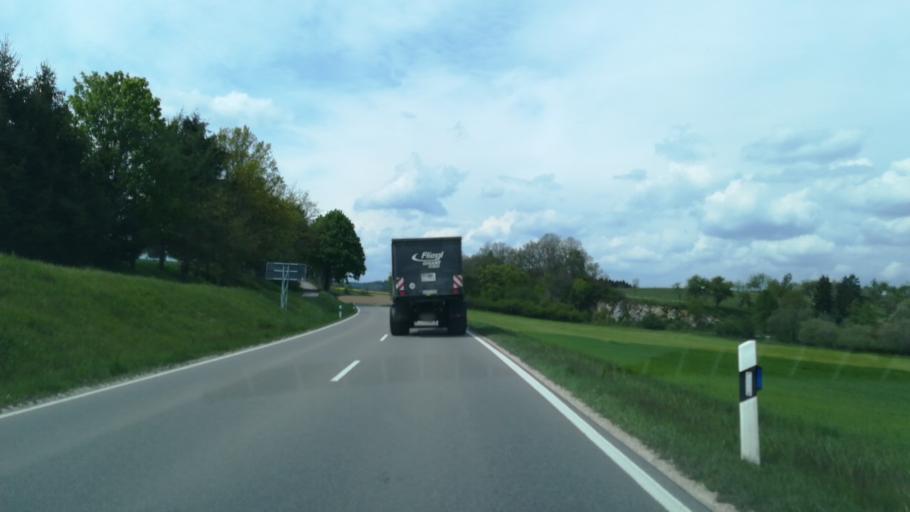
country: DE
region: Baden-Wuerttemberg
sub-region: Tuebingen Region
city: Messkirch
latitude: 48.0105
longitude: 9.1143
